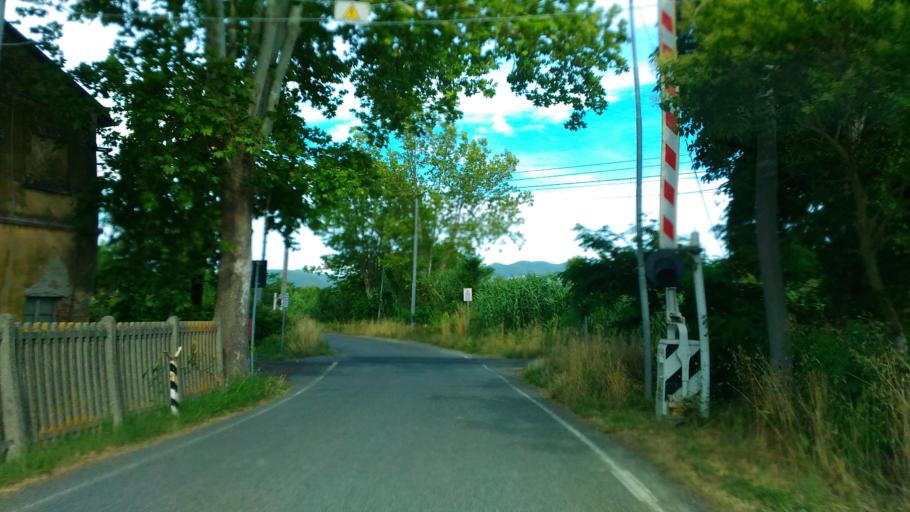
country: IT
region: Tuscany
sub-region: Provincia di Livorno
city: Rosignano Marittimo
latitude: 43.4372
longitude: 10.4891
